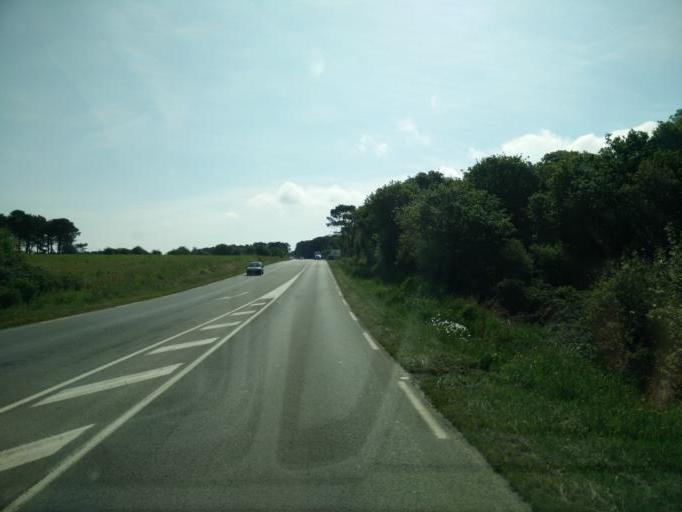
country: FR
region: Brittany
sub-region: Departement du Finistere
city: Crozon
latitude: 48.2485
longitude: -4.4522
